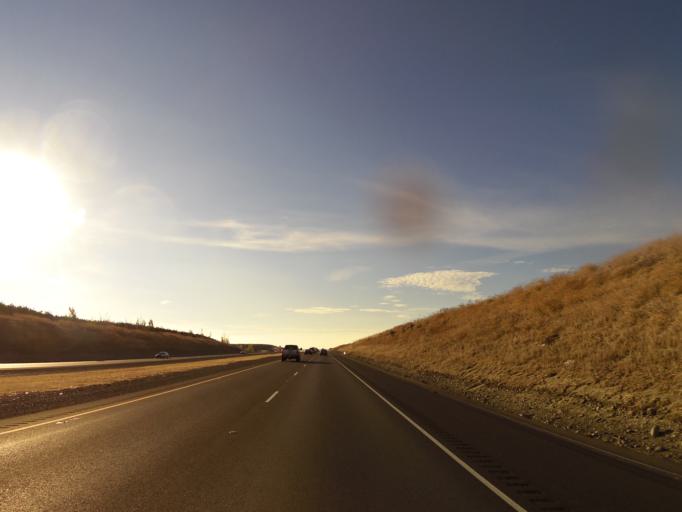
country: US
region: California
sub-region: Stanislaus County
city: Newman
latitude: 37.3476
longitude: -121.1174
